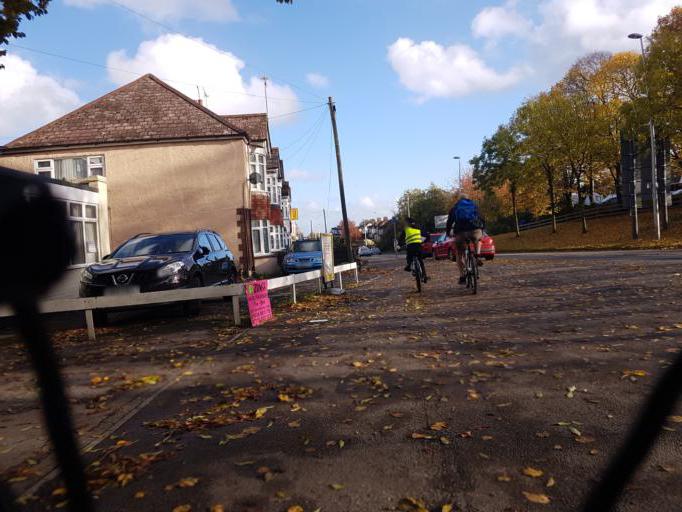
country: GB
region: England
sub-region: Kent
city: Rainham
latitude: 51.3684
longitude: 0.5830
